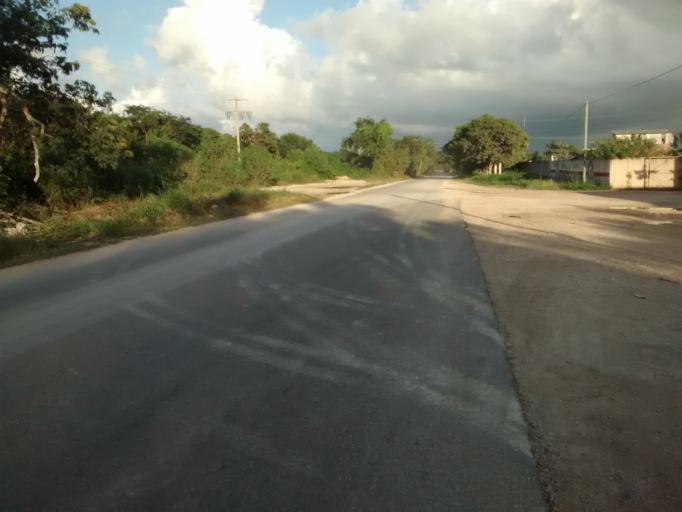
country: MX
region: Yucatan
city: Valladolid
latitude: 20.7311
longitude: -88.2073
